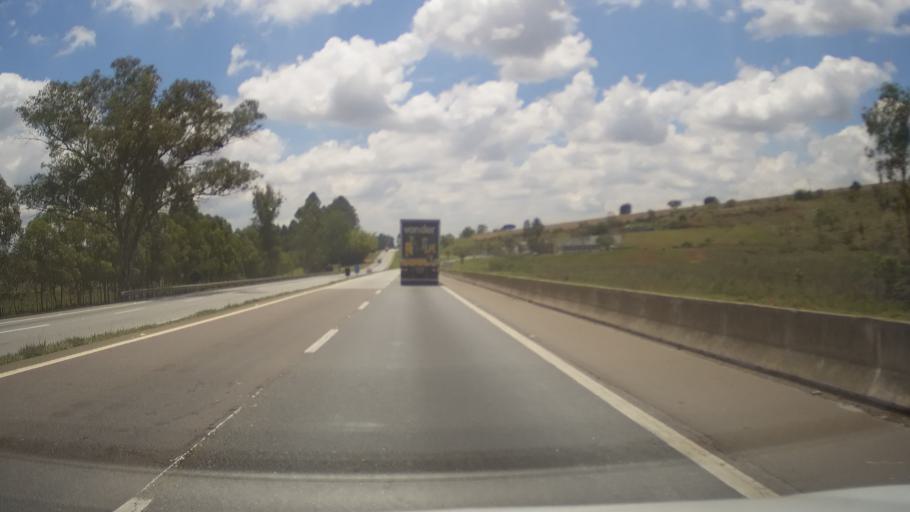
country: BR
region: Minas Gerais
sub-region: Campanha
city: Campanha
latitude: -21.7955
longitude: -45.4536
